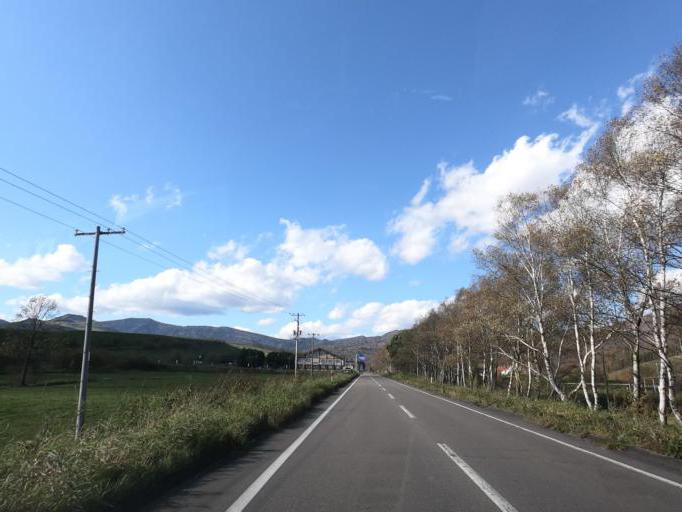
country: JP
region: Hokkaido
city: Otofuke
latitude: 43.2823
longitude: 143.2395
